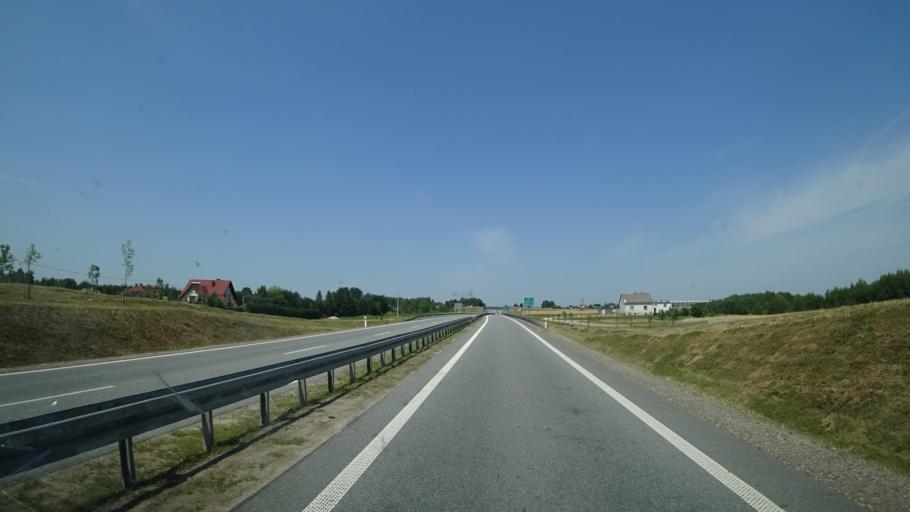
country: PL
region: Pomeranian Voivodeship
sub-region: Powiat koscierski
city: Koscierzyna
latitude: 54.1281
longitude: 18.0179
